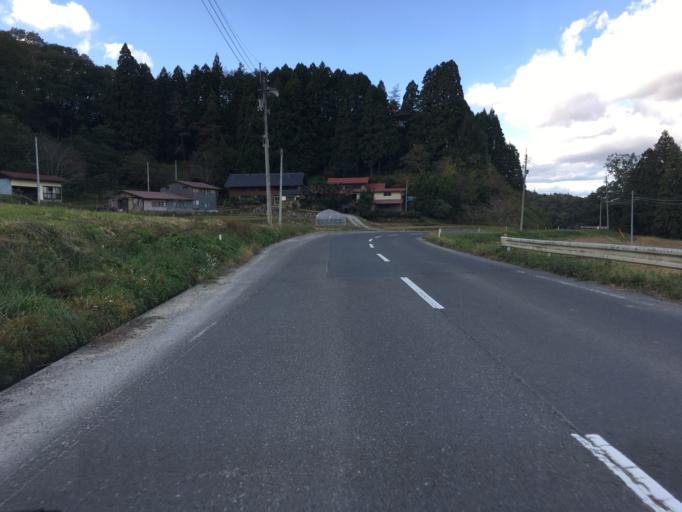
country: JP
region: Miyagi
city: Marumori
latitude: 37.8359
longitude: 140.8325
